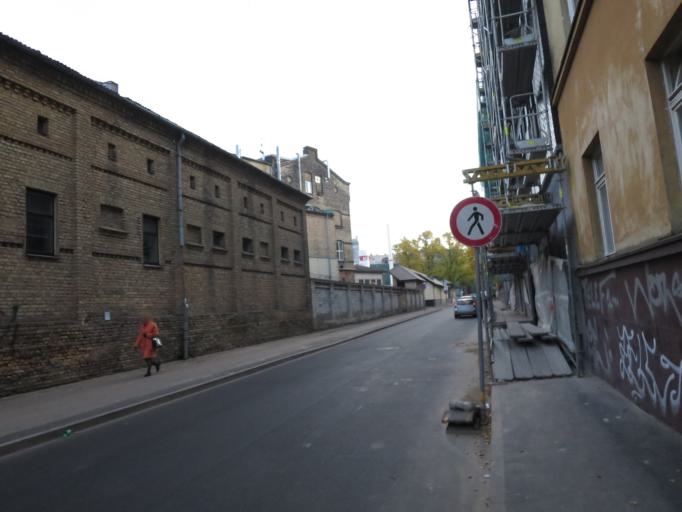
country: LV
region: Riga
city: Riga
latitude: 56.9644
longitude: 24.1285
